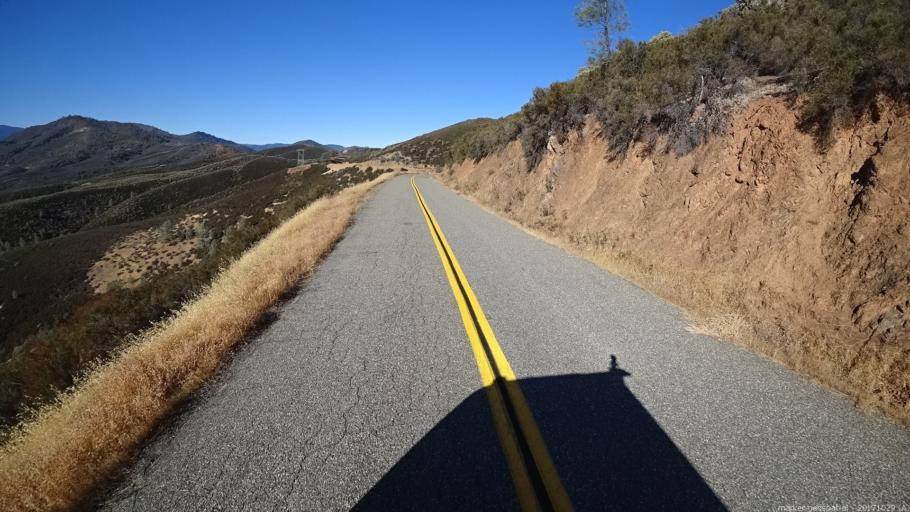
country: US
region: California
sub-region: Trinity County
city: Lewiston
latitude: 40.3642
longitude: -122.8581
